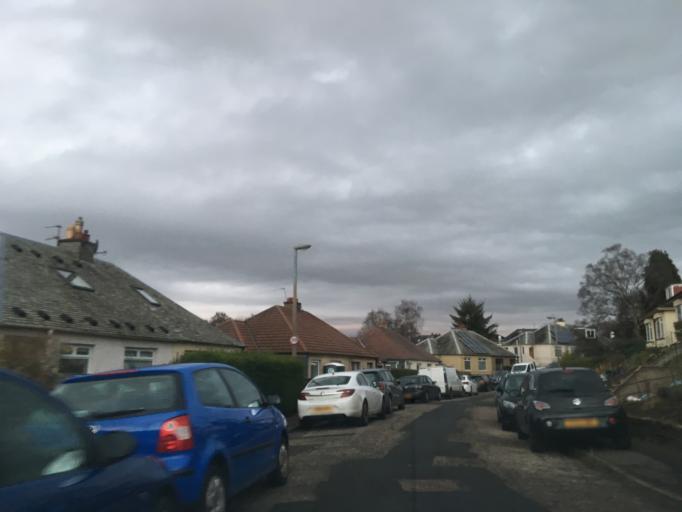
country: GB
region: Scotland
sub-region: Edinburgh
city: Colinton
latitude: 55.9188
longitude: -3.2625
